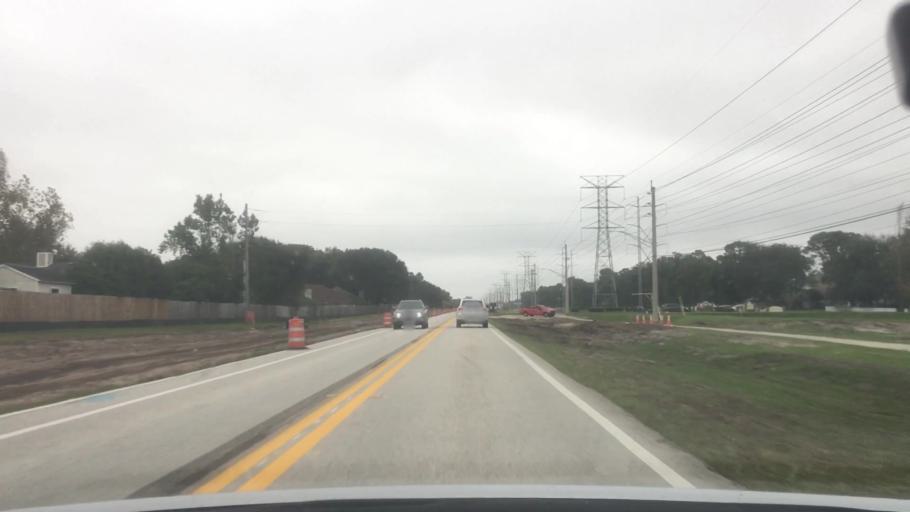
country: US
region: Florida
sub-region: Duval County
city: Atlantic Beach
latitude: 30.3496
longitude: -81.4899
